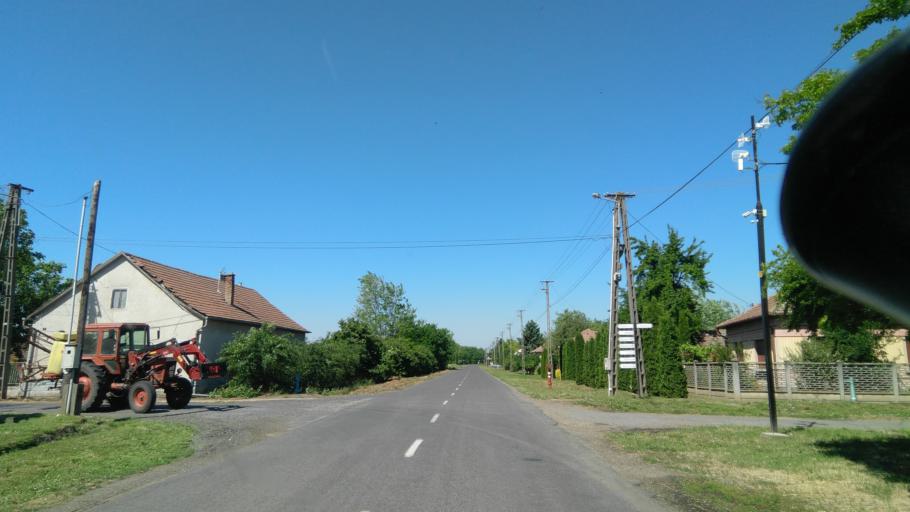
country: HU
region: Bekes
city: Kevermes
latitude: 46.4230
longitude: 21.1191
